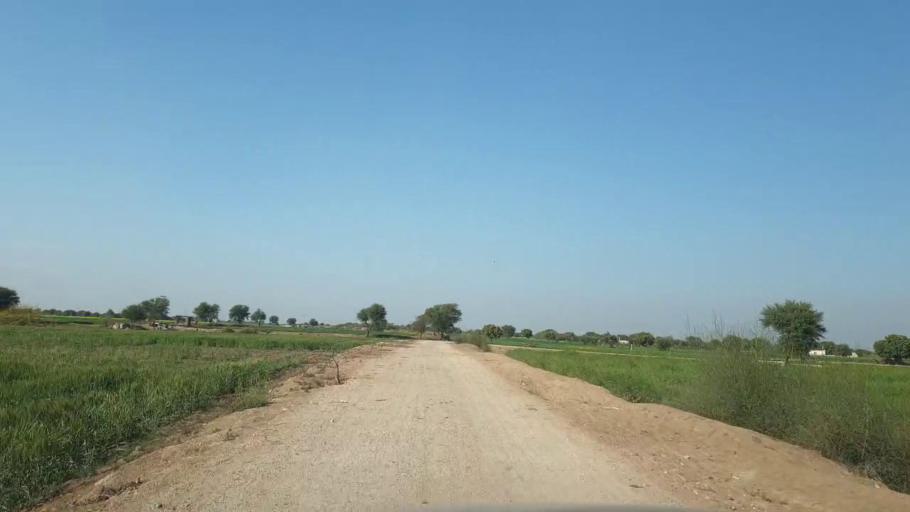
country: PK
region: Sindh
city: Tando Adam
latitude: 25.6649
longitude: 68.6930
